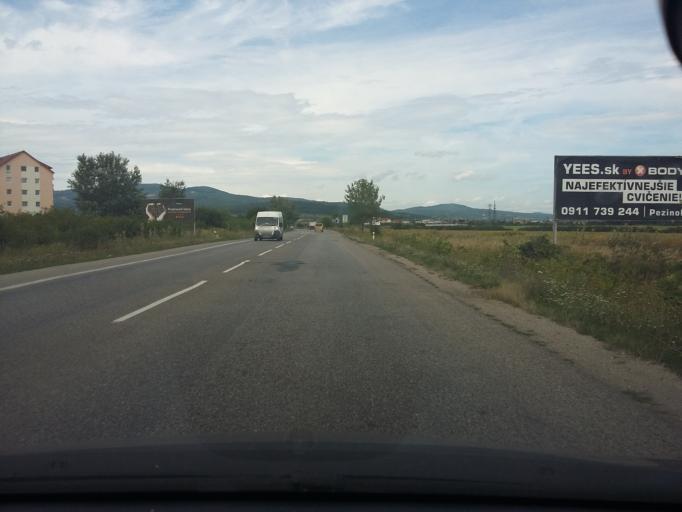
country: SK
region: Bratislavsky
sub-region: Okres Pezinok
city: Pezinok
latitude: 48.2948
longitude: 17.2809
